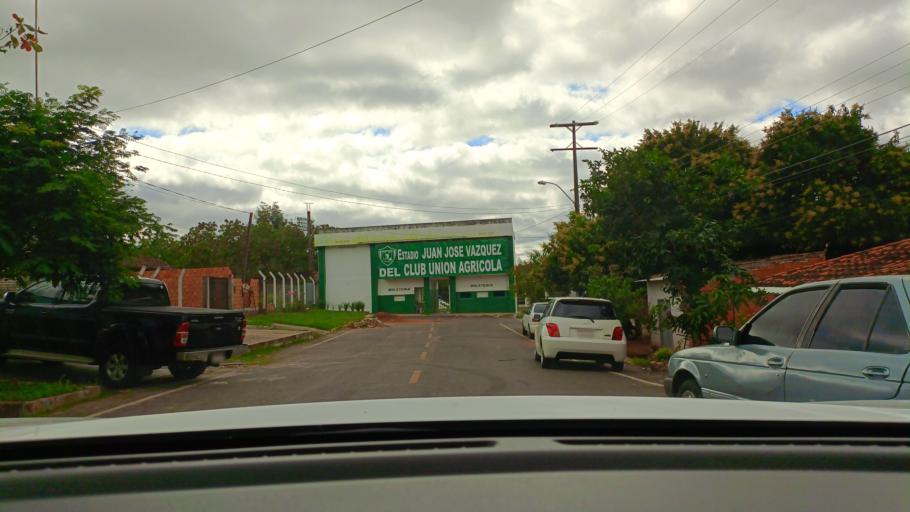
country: PY
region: San Pedro
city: Guayaybi
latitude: -24.6580
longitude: -56.4422
